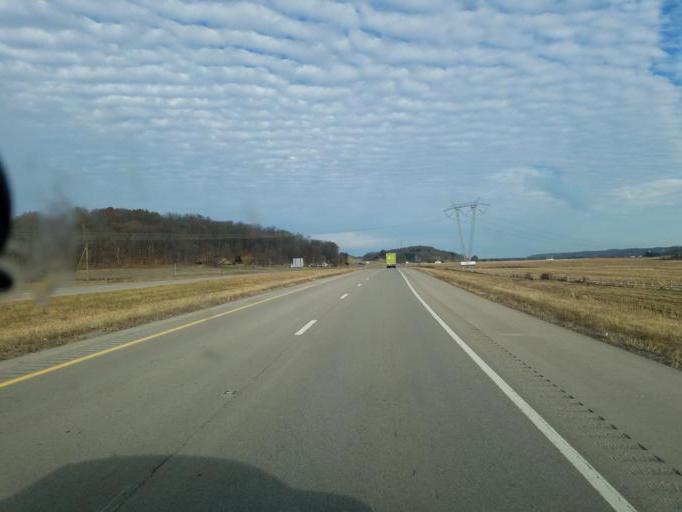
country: US
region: Ohio
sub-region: Muskingum County
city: Frazeysburg
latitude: 40.1099
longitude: -82.1676
